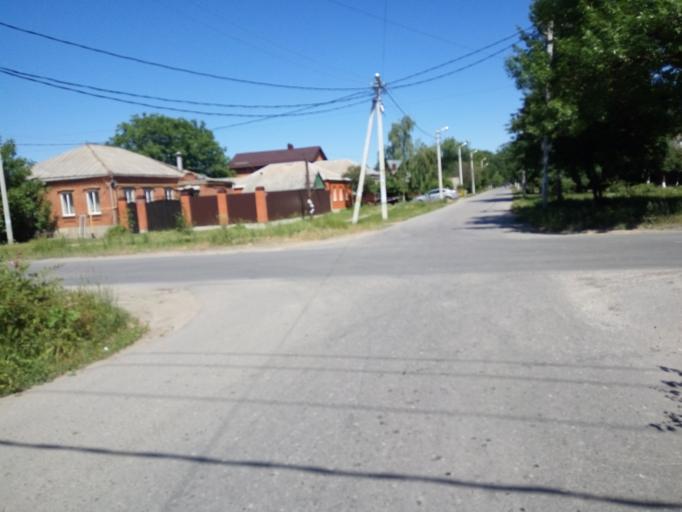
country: RU
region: Rostov
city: Bataysk
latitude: 47.1236
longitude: 39.7473
